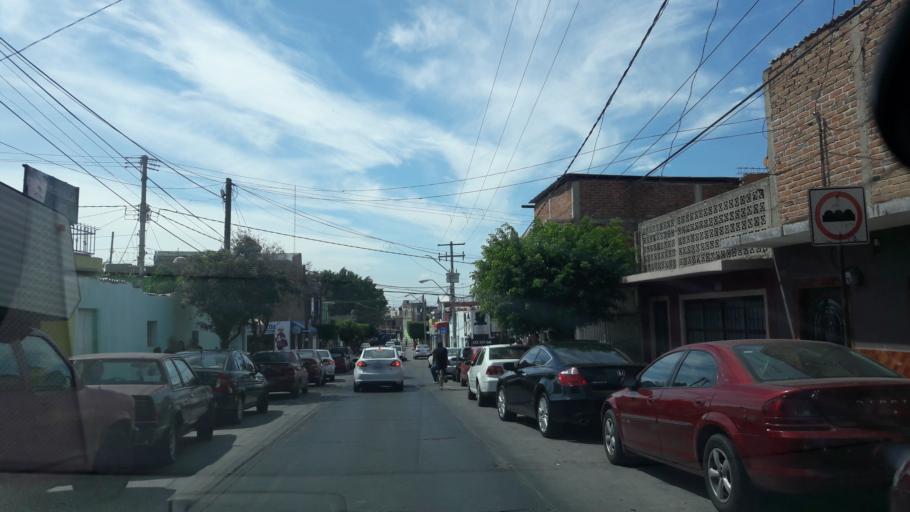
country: MX
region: Guanajuato
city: Leon
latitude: 21.1111
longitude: -101.6999
